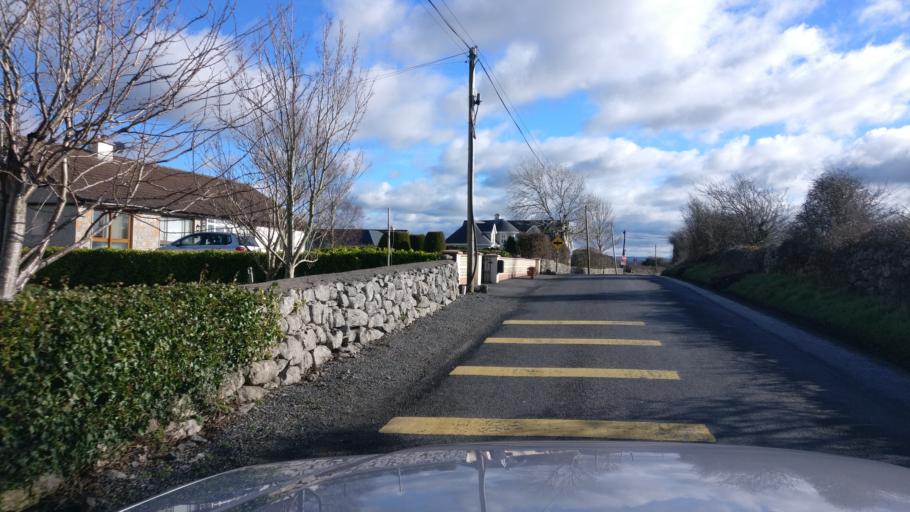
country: IE
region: Connaught
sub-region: County Galway
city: Oranmore
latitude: 53.2509
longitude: -8.8463
